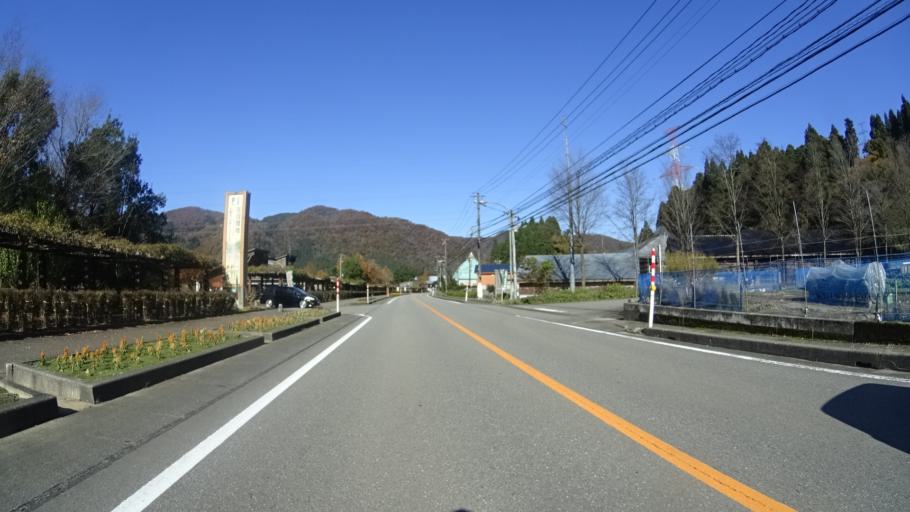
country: JP
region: Ishikawa
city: Tsurugi-asahimachi
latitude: 36.3804
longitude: 136.6147
